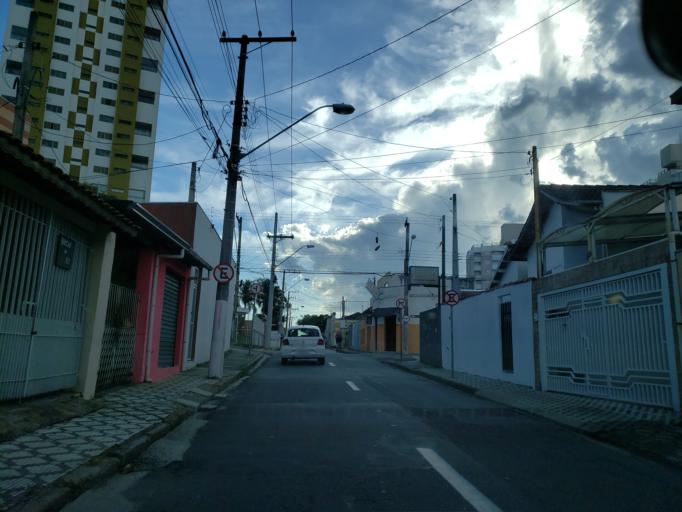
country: BR
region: Sao Paulo
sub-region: Taubate
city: Taubate
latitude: -23.0355
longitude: -45.5658
